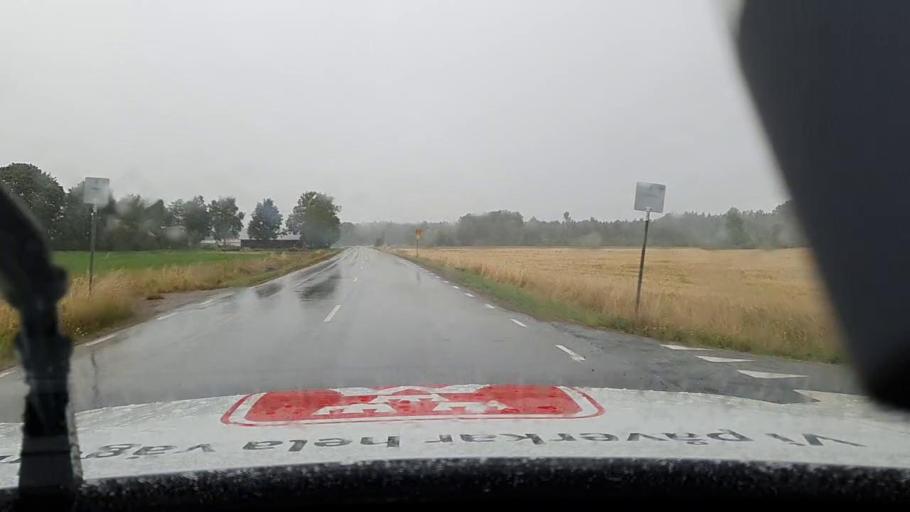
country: SE
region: Vaestra Goetaland
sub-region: Toreboda Kommun
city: Toereboda
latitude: 58.6756
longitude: 14.1339
